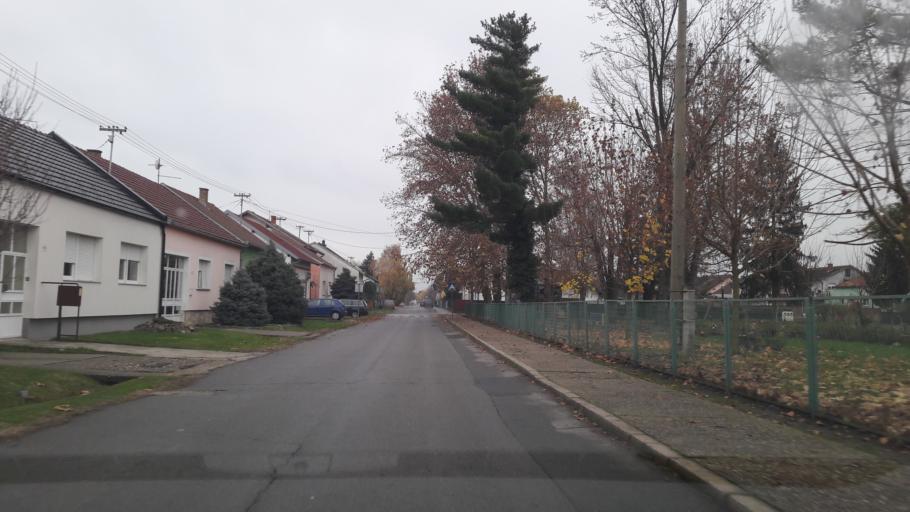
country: HR
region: Osjecko-Baranjska
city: Visnjevac
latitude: 45.5656
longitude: 18.6123
